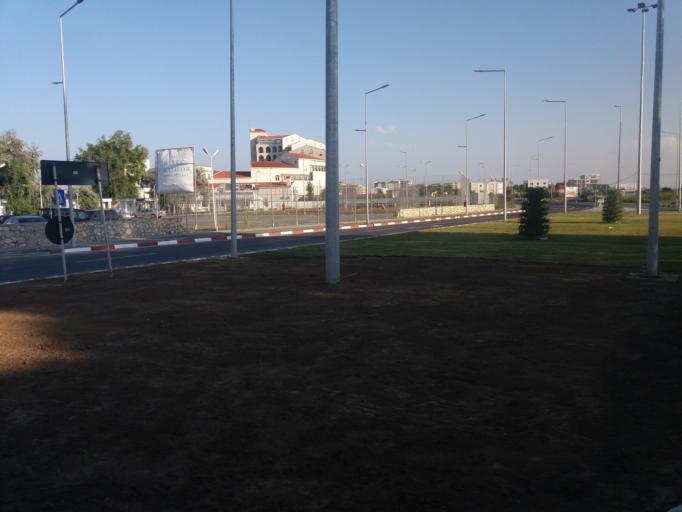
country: RO
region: Constanta
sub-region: Comuna Navodari
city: Navodari
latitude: 44.2882
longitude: 28.6165
